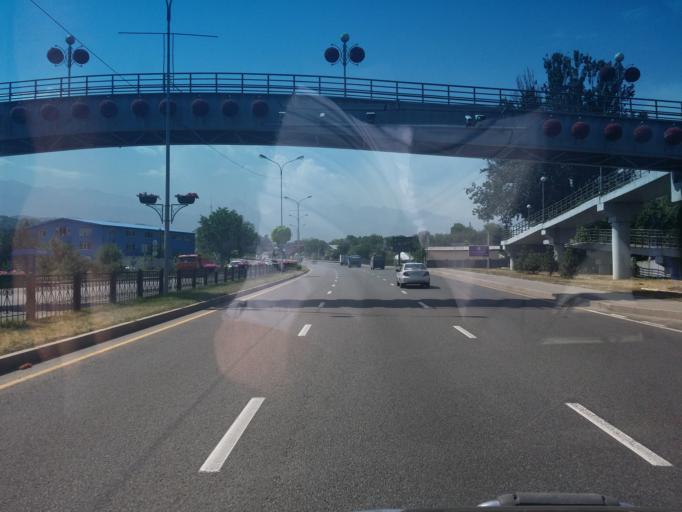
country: KZ
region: Almaty Qalasy
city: Almaty
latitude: 43.2799
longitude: 76.9853
